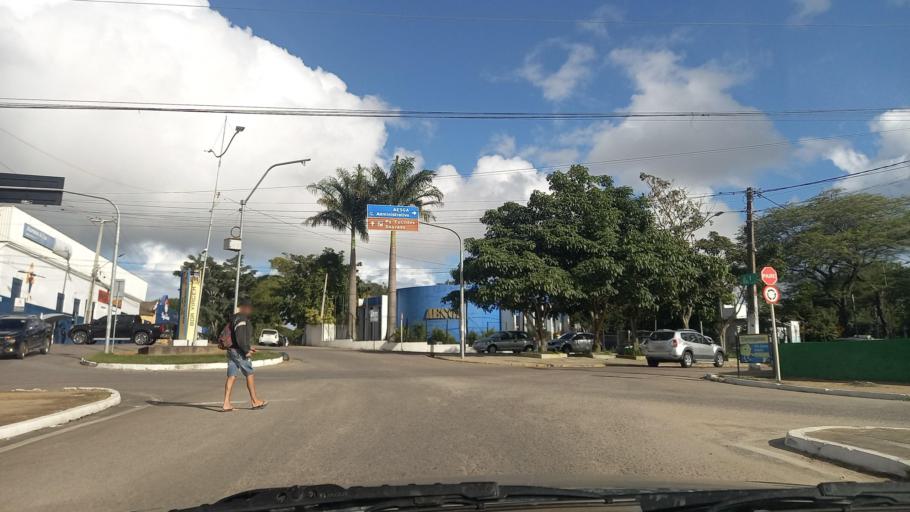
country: BR
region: Pernambuco
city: Garanhuns
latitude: -8.8795
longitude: -36.4856
